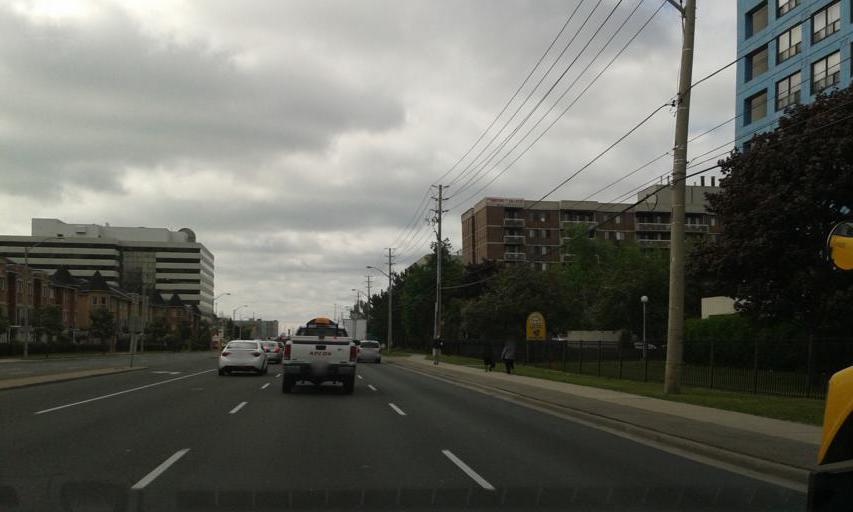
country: CA
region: Ontario
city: Scarborough
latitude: 43.7922
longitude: -79.2382
